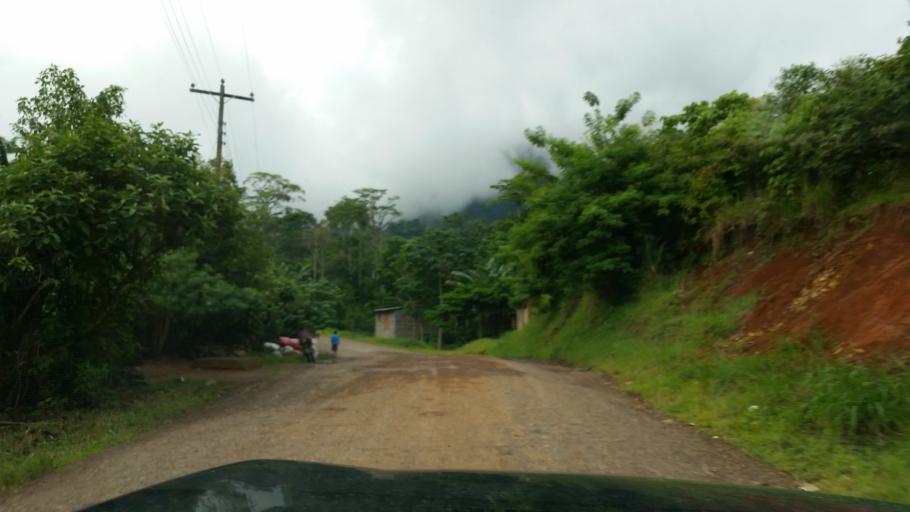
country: NI
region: Jinotega
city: Jinotega
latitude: 13.2744
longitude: -85.7288
